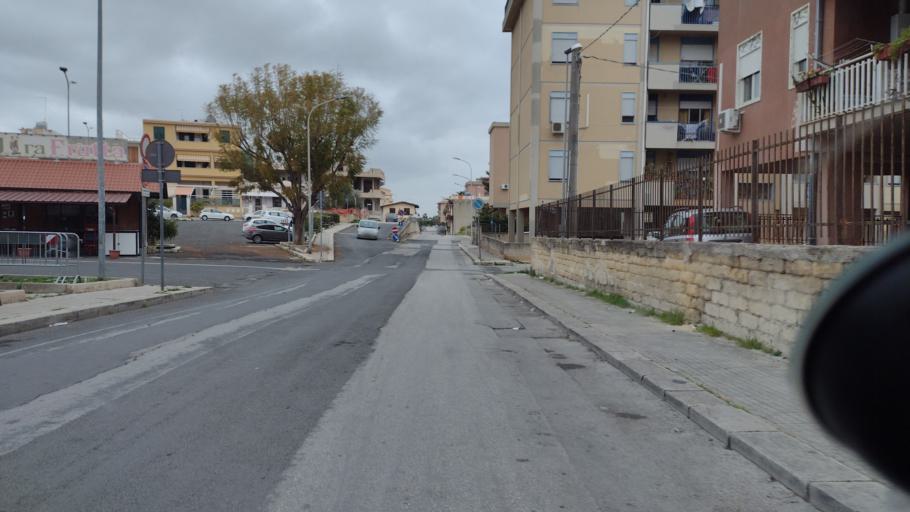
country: IT
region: Sicily
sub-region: Provincia di Siracusa
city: Avola
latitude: 36.9144
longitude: 15.1382
